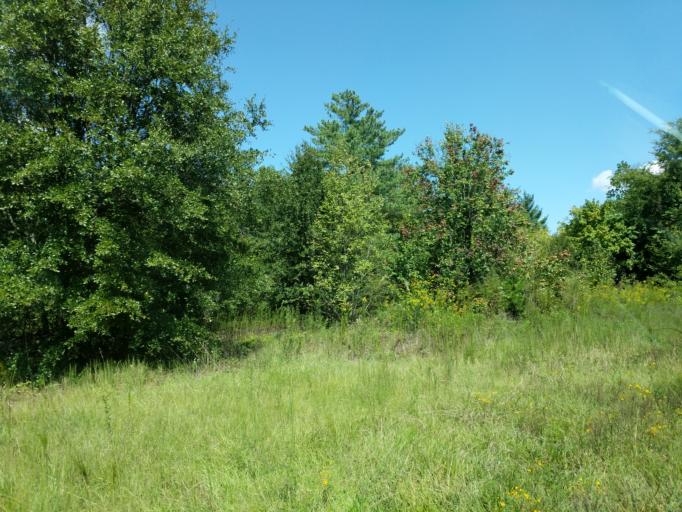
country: US
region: South Carolina
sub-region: Spartanburg County
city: Valley Falls
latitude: 35.0184
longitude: -81.9289
